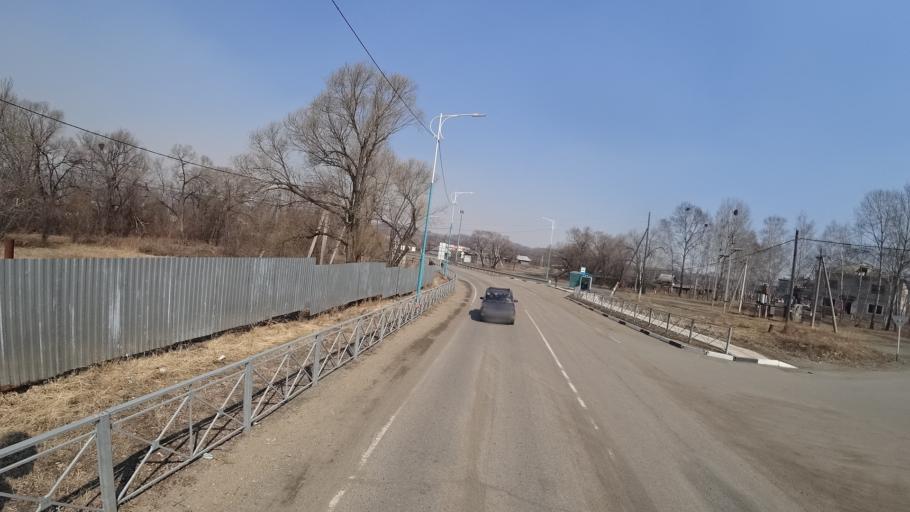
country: RU
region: Amur
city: Novobureyskiy
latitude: 49.7928
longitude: 129.9054
